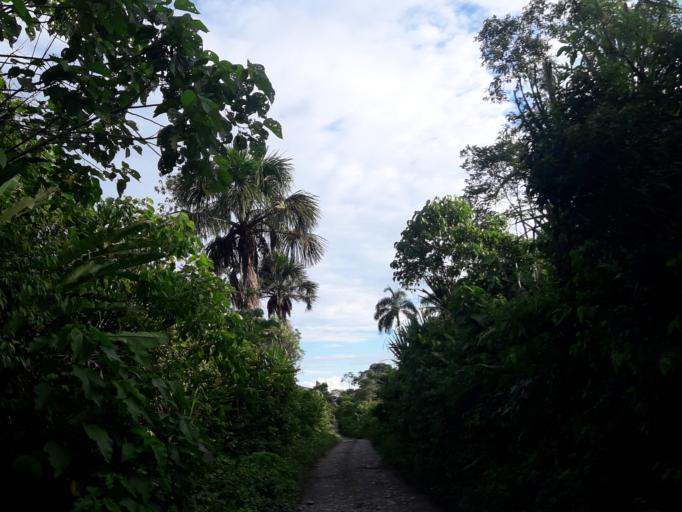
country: EC
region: Orellana
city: Boca Suno
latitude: -0.8908
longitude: -77.3064
